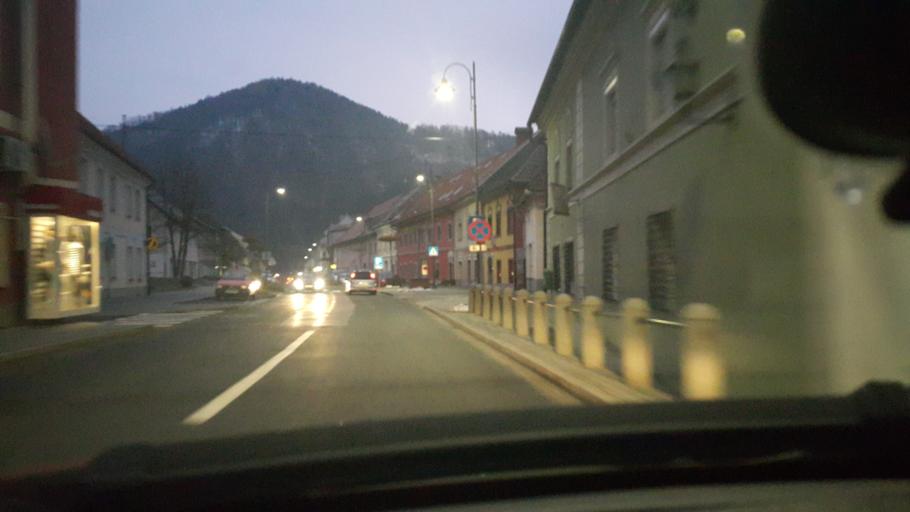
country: SI
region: Dravograd
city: Dravograd
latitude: 46.5902
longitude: 15.0179
